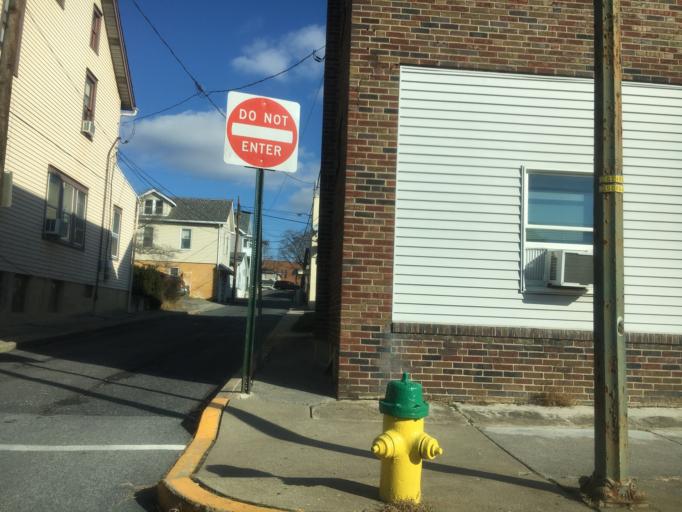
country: US
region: Pennsylvania
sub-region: Northampton County
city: Northampton
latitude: 40.6854
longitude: -75.4960
